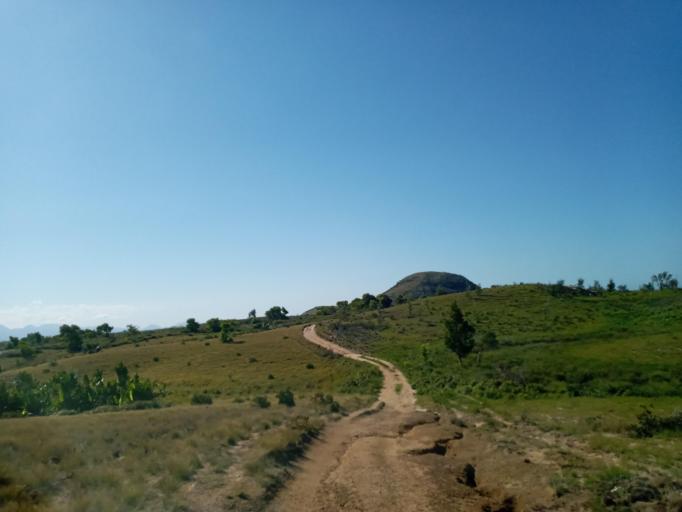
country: MG
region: Anosy
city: Fort Dauphin
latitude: -24.9084
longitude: 47.0906
